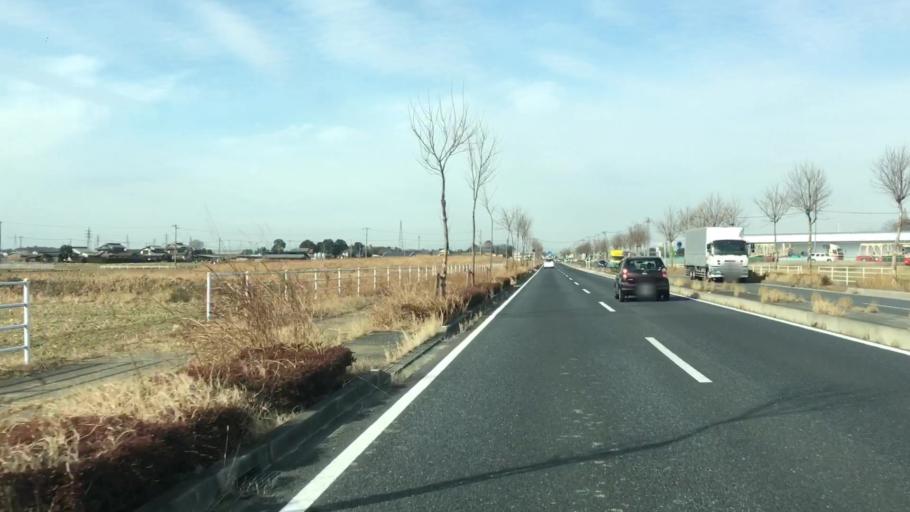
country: JP
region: Gunma
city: Tatebayashi
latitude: 36.2301
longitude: 139.4900
